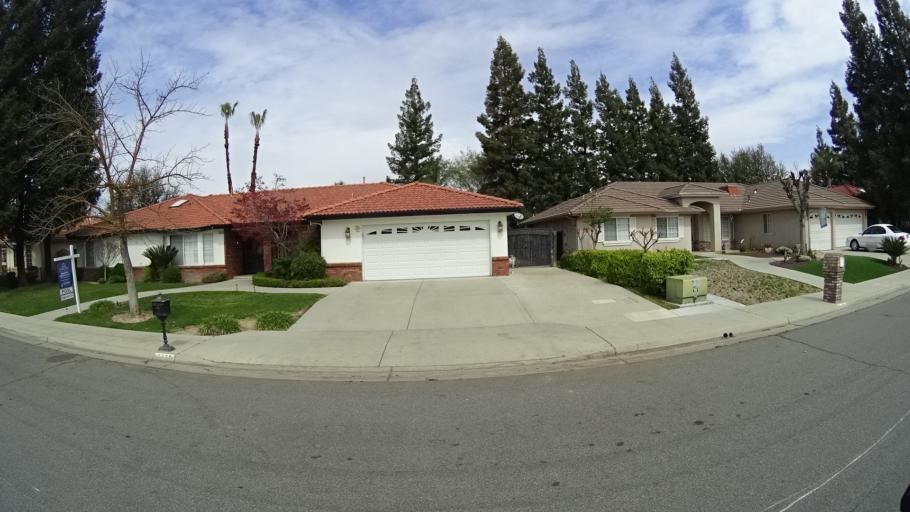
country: US
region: California
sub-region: Fresno County
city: Biola
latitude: 36.8419
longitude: -119.8873
